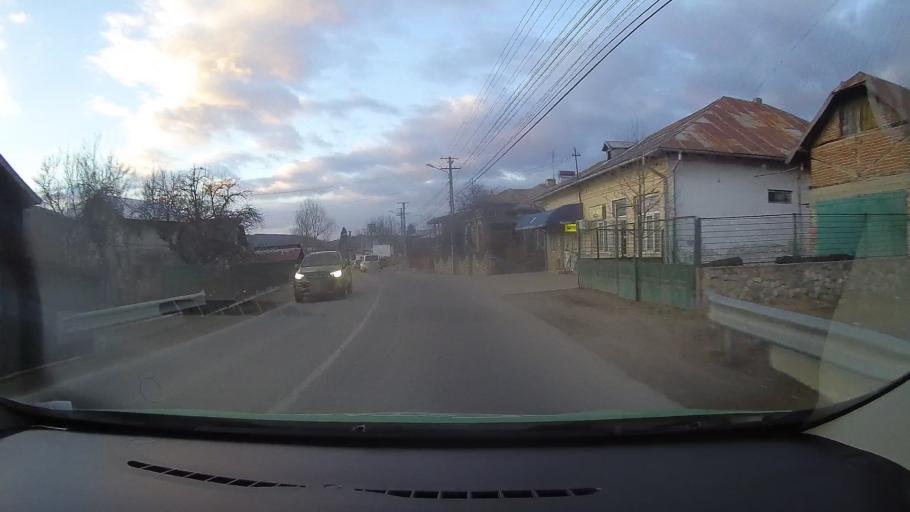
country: RO
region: Dambovita
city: Iedera de Jos
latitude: 45.0197
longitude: 25.6380
